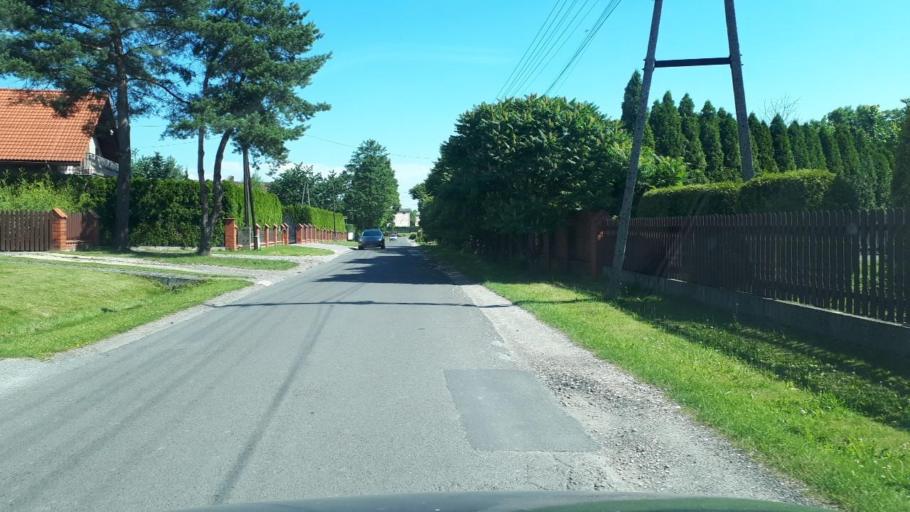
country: PL
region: Silesian Voivodeship
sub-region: Powiat pszczynski
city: Jankowice
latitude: 49.9753
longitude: 18.9822
